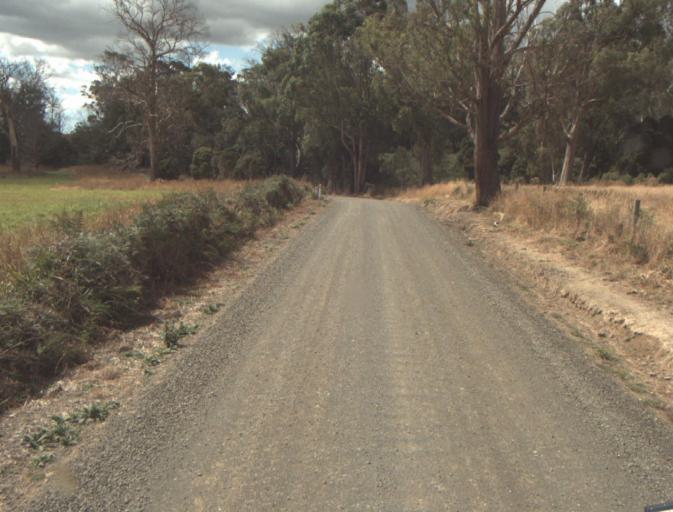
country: AU
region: Tasmania
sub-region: Launceston
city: Mayfield
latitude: -41.3041
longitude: 146.9953
